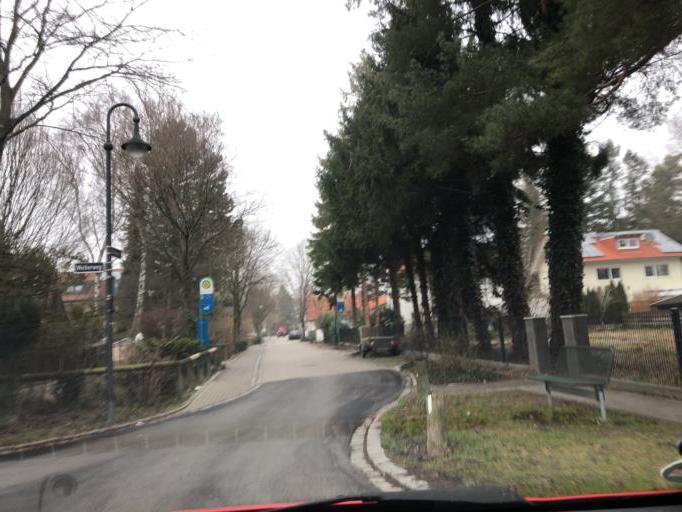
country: DE
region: Bavaria
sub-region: Upper Bavaria
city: Grobenzell
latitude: 48.2023
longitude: 11.3792
